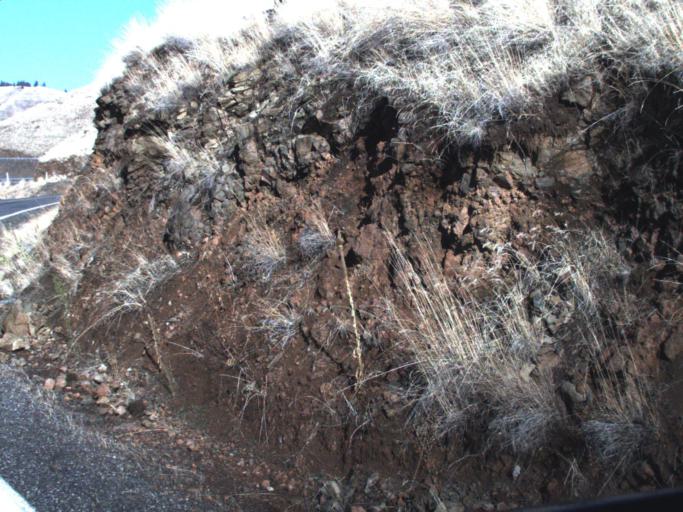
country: US
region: Washington
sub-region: Asotin County
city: Asotin
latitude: 46.0583
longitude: -117.2322
